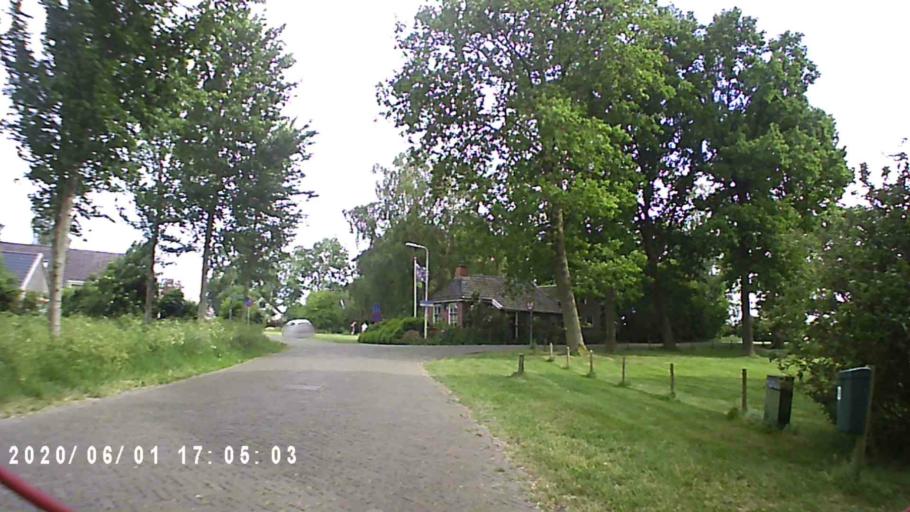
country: NL
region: Friesland
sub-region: Gemeente Tytsjerksteradiel
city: Garyp
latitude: 53.1725
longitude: 5.9341
